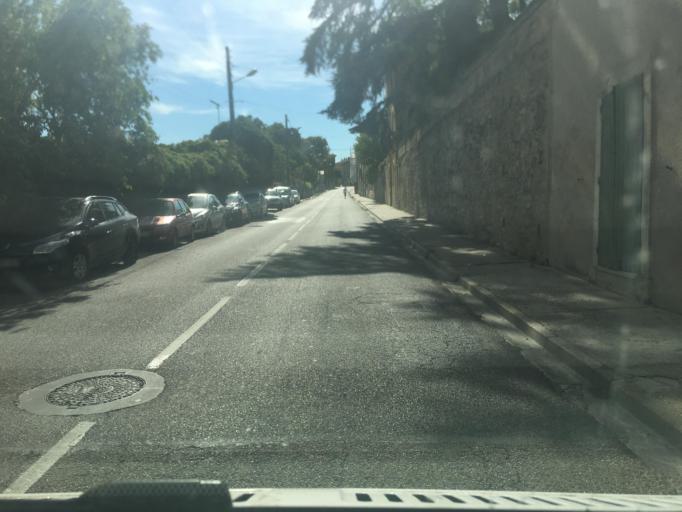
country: FR
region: Languedoc-Roussillon
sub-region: Departement du Gard
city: Uzes
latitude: 44.0153
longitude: 4.4245
